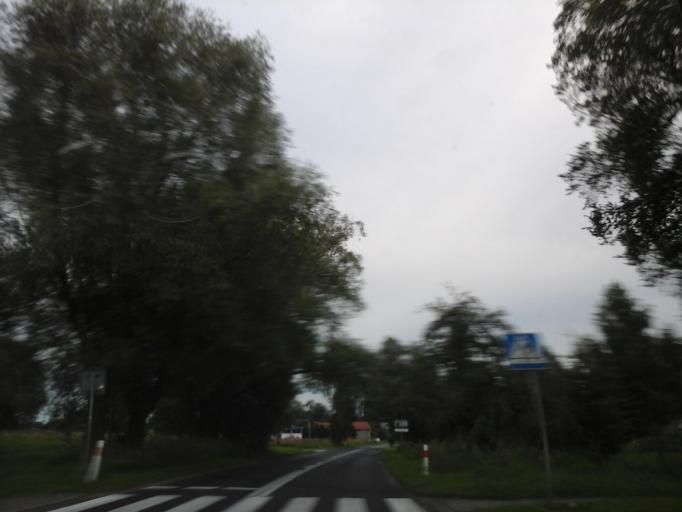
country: PL
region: West Pomeranian Voivodeship
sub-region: Powiat goleniowski
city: Maszewo
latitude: 53.4971
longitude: 15.0659
